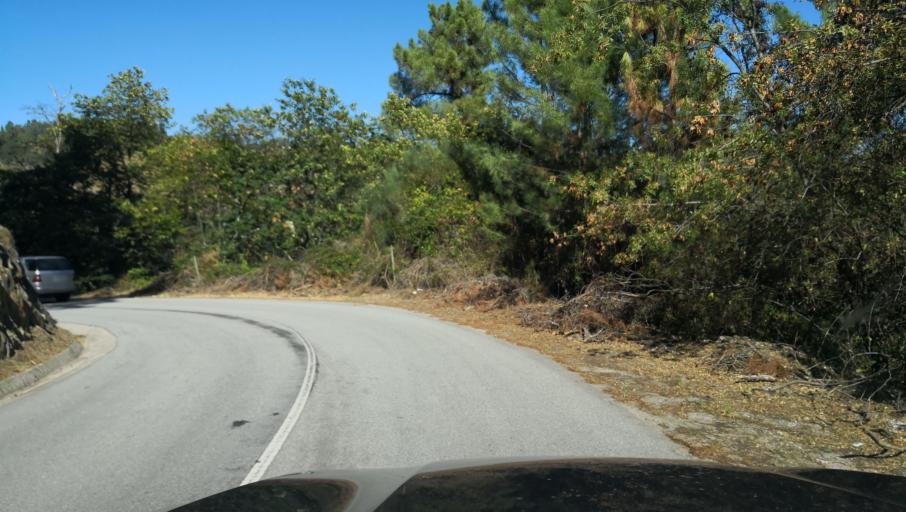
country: PT
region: Vila Real
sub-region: Santa Marta de Penaguiao
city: Santa Marta de Penaguiao
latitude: 41.2390
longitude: -7.8019
